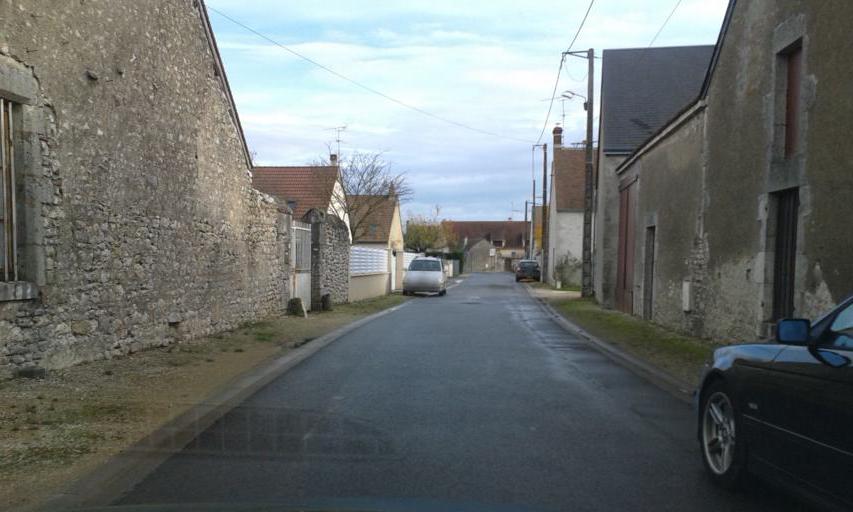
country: FR
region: Centre
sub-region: Departement du Loiret
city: Beaugency
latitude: 47.8110
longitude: 1.6368
